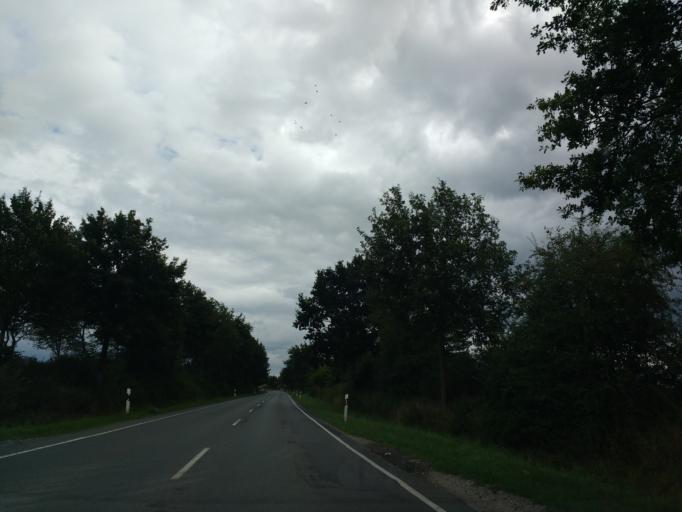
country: DE
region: Lower Saxony
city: Bad Laer
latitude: 52.0982
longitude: 8.0768
